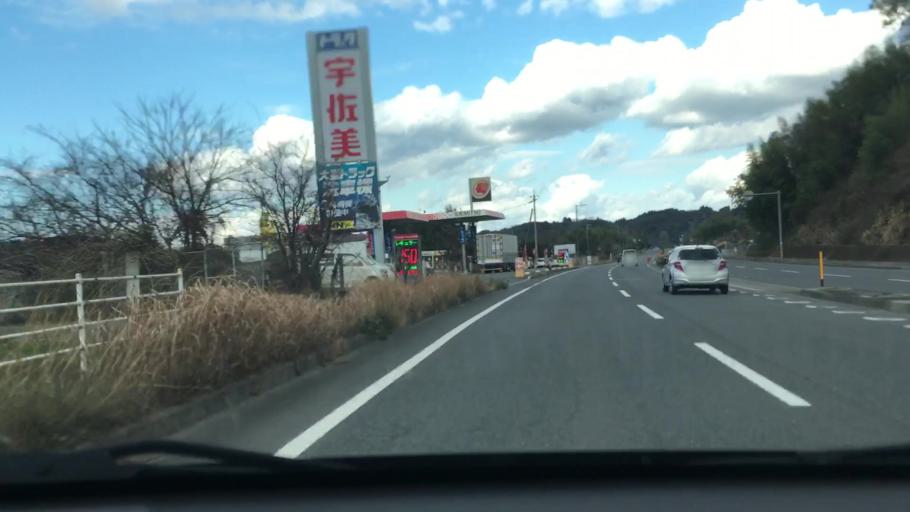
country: JP
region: Oita
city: Oita
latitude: 33.1246
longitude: 131.6549
